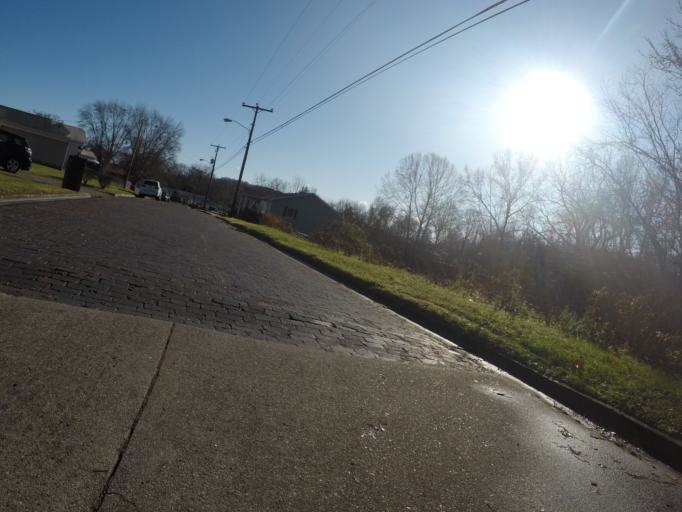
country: US
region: Ohio
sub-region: Lawrence County
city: Burlington
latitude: 38.4002
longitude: -82.5253
